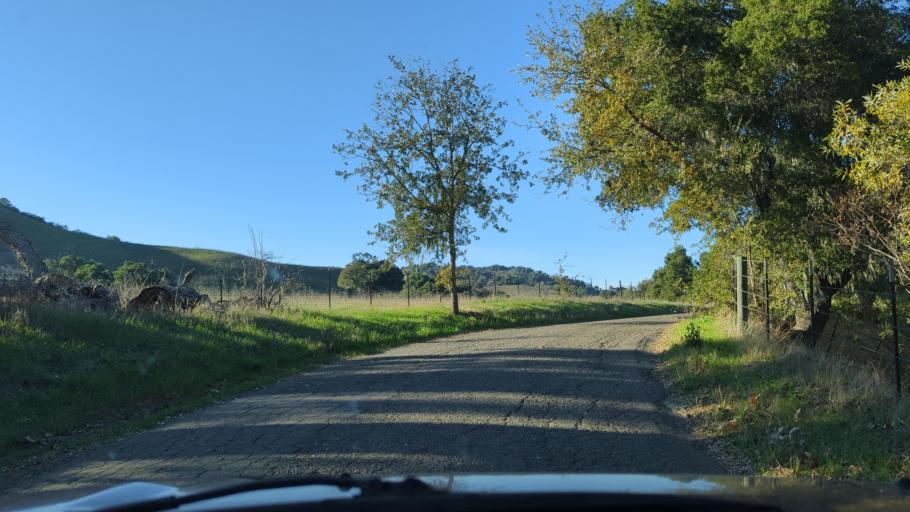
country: US
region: California
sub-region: Santa Barbara County
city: Santa Ynez
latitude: 34.5627
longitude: -120.0902
